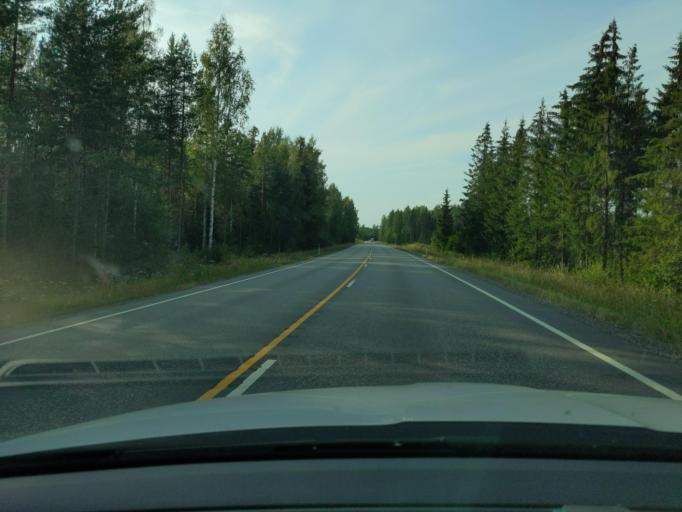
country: FI
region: Paijanne Tavastia
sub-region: Lahti
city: Padasjoki
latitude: 61.3170
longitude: 25.2877
